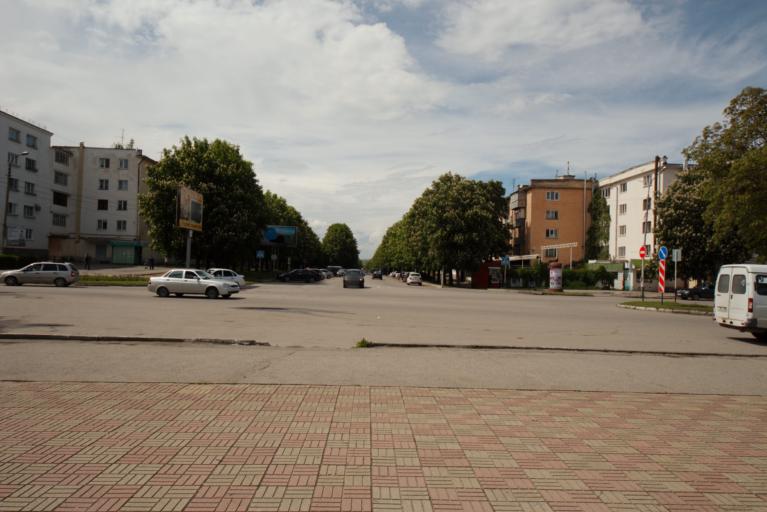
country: RU
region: Kabardino-Balkariya
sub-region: Gorod Nal'chik
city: Nal'chik
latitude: 43.4783
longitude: 43.5870
